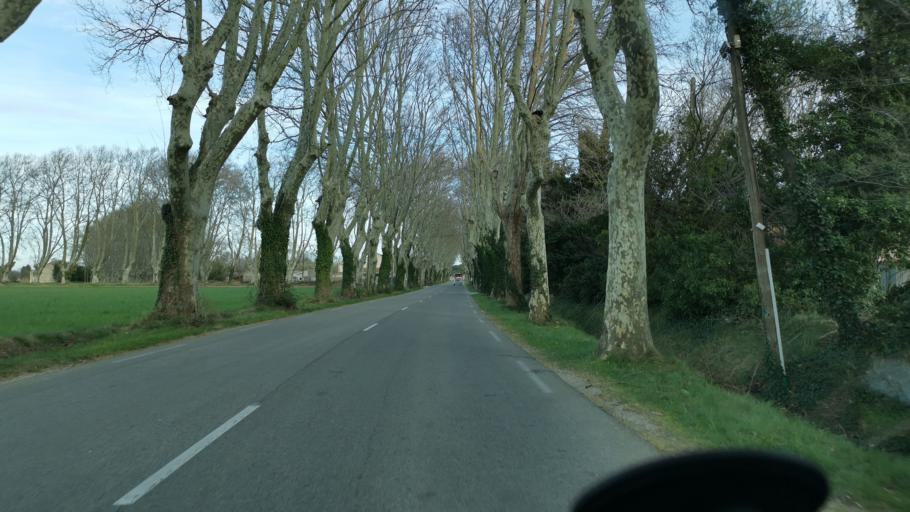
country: FR
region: Provence-Alpes-Cote d'Azur
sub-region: Departement des Bouches-du-Rhone
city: Saint-Martin-de-Crau
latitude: 43.6355
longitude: 4.7602
